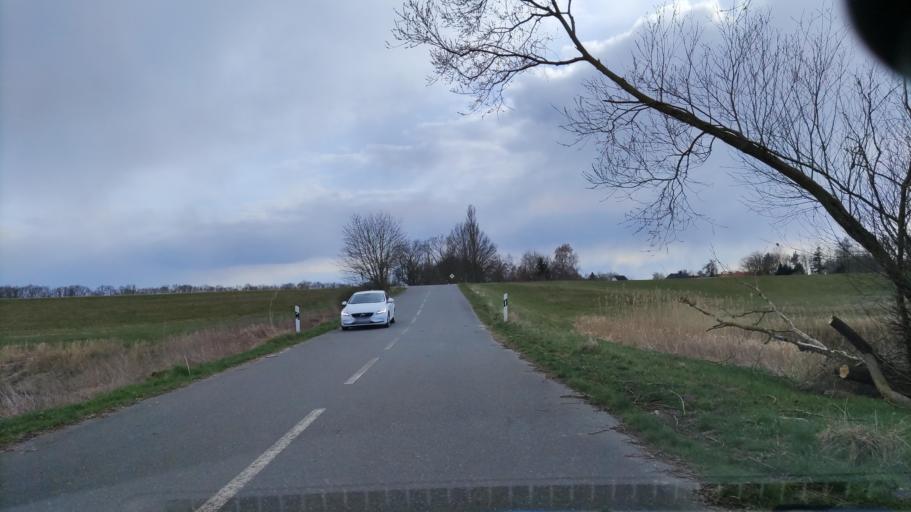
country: DE
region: Mecklenburg-Vorpommern
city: Domitz
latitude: 53.1326
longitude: 11.2371
